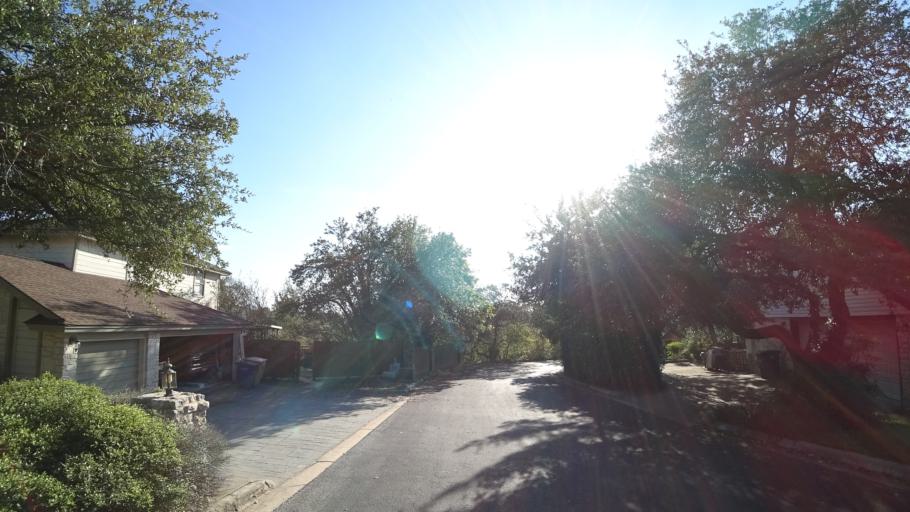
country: US
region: Texas
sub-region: Williamson County
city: Anderson Mill
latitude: 30.4296
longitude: -97.8129
